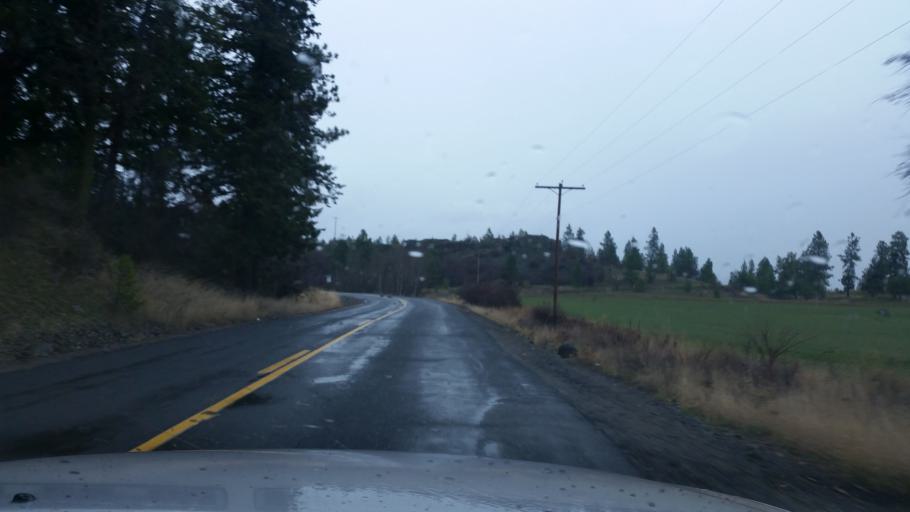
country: US
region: Washington
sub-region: Spokane County
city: Airway Heights
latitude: 47.6961
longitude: -117.5719
